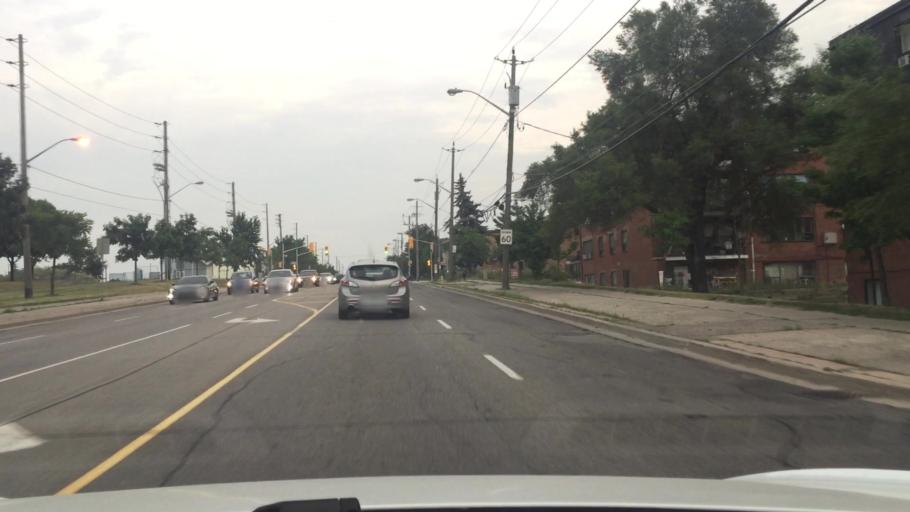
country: CA
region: Ontario
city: Concord
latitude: 43.7382
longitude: -79.4849
